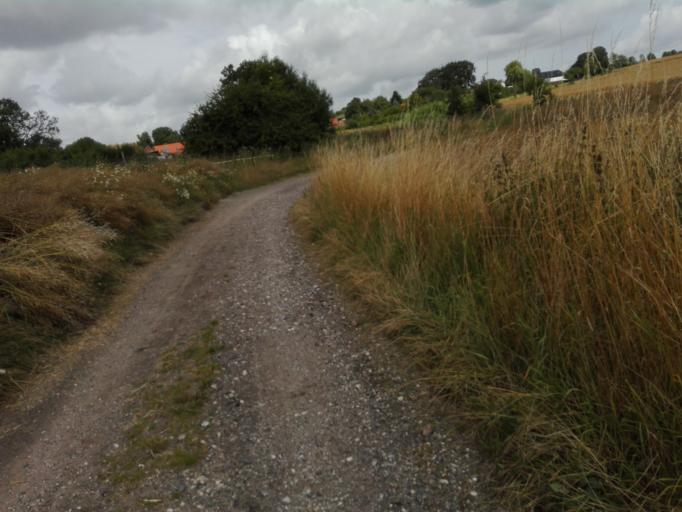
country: DK
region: Central Jutland
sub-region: Arhus Kommune
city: Marslet
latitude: 56.0816
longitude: 10.1818
